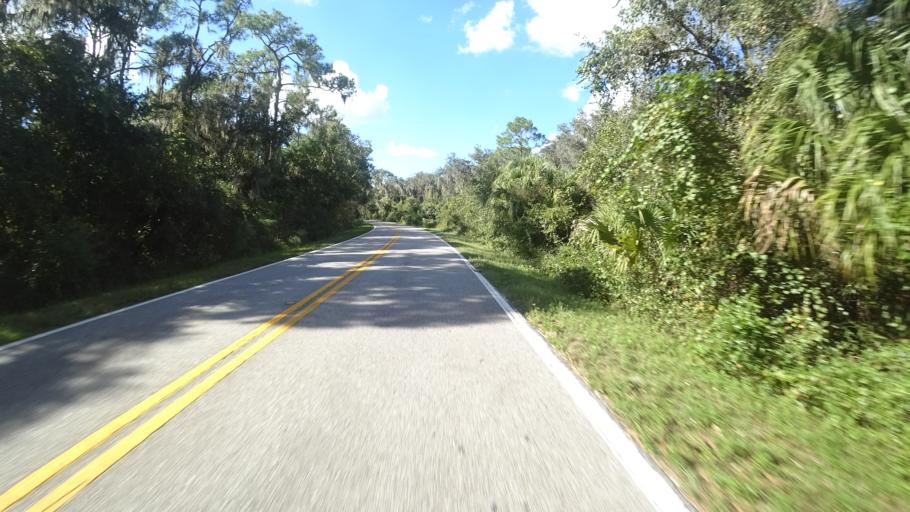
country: US
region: Florida
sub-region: Sarasota County
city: Lake Sarasota
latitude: 27.3051
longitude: -82.2590
